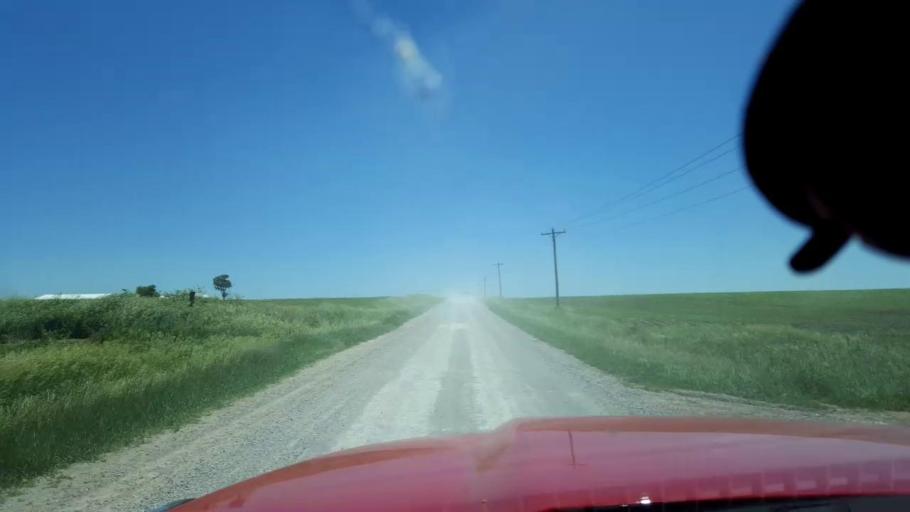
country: US
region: Iowa
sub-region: Washington County
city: Washington
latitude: 41.2799
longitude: -91.6499
